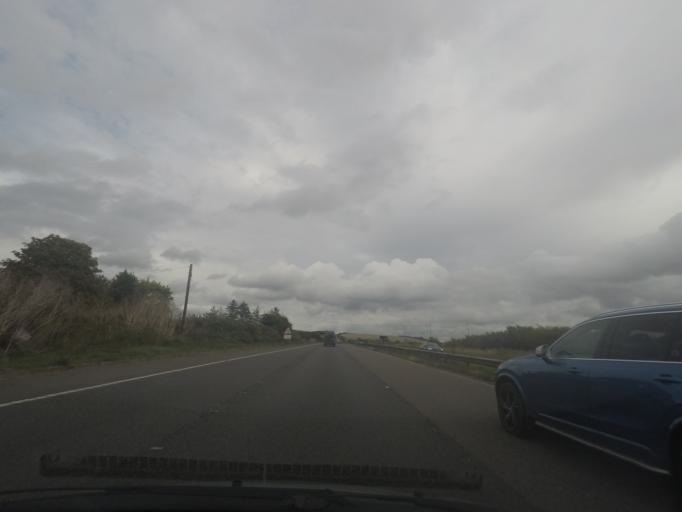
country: GB
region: England
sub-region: Wiltshire
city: Bulford
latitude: 51.1785
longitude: -1.7549
